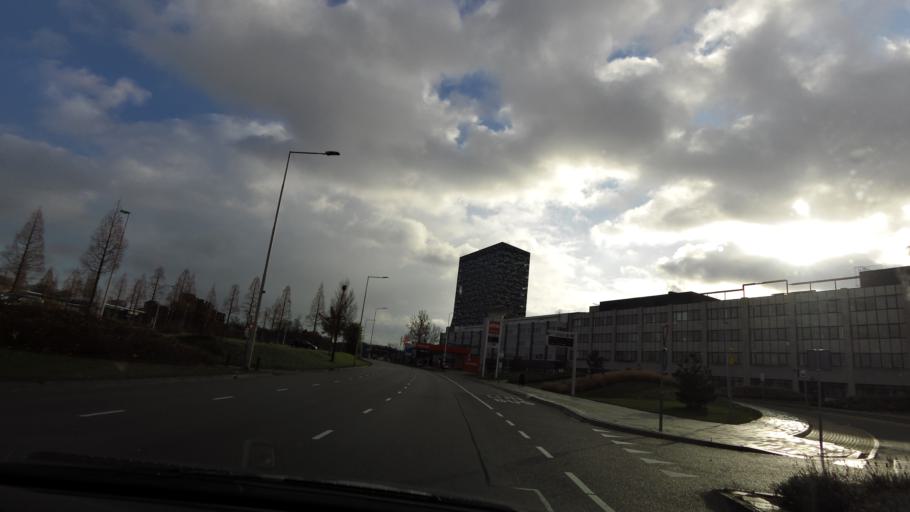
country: NL
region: Gelderland
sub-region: Gemeente Nijmegen
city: Lindenholt
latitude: 51.8272
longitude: 5.8231
